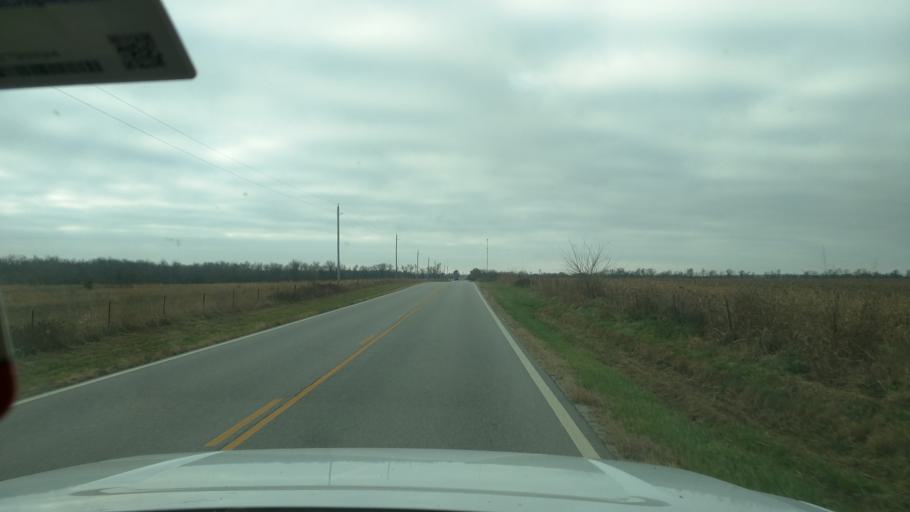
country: US
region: Kansas
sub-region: Elk County
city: Howard
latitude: 37.6471
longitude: -96.2346
